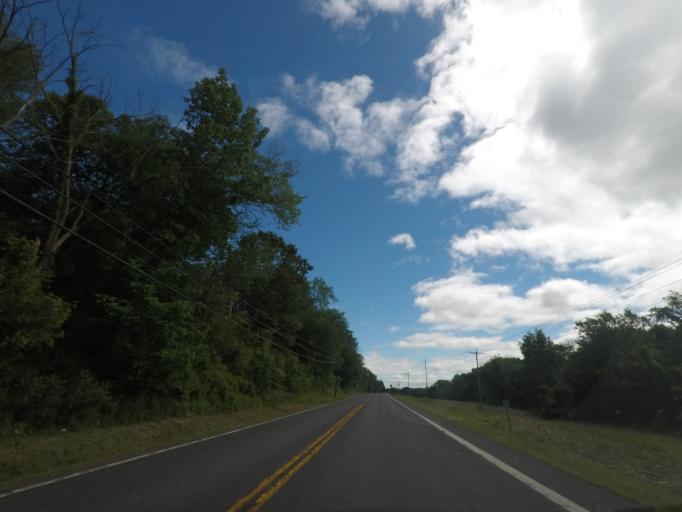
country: US
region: Massachusetts
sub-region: Berkshire County
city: Great Barrington
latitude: 42.1493
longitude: -73.5207
